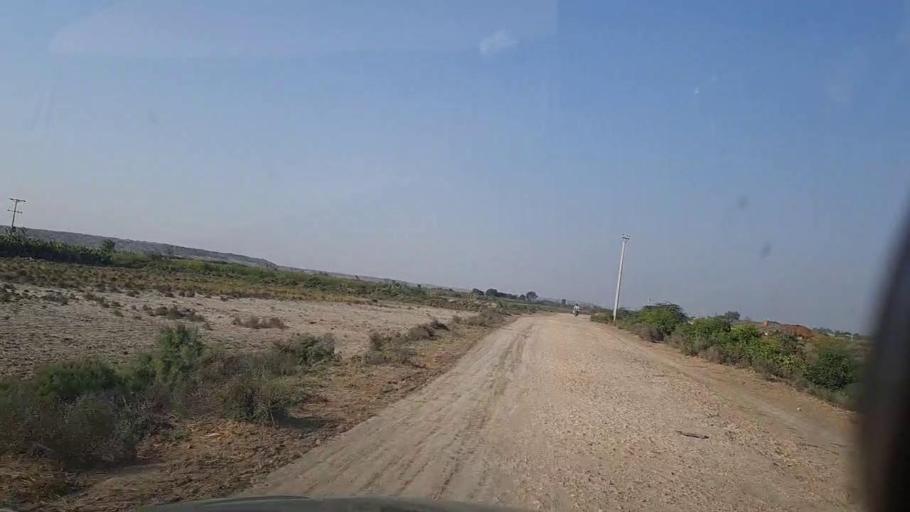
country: PK
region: Sindh
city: Thatta
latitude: 24.5977
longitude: 67.8744
